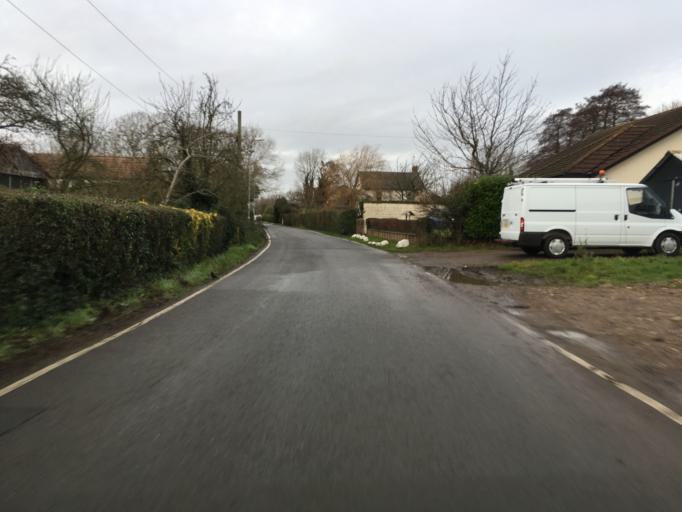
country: GB
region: Wales
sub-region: Monmouthshire
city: Magor
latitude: 51.5741
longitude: -2.8234
